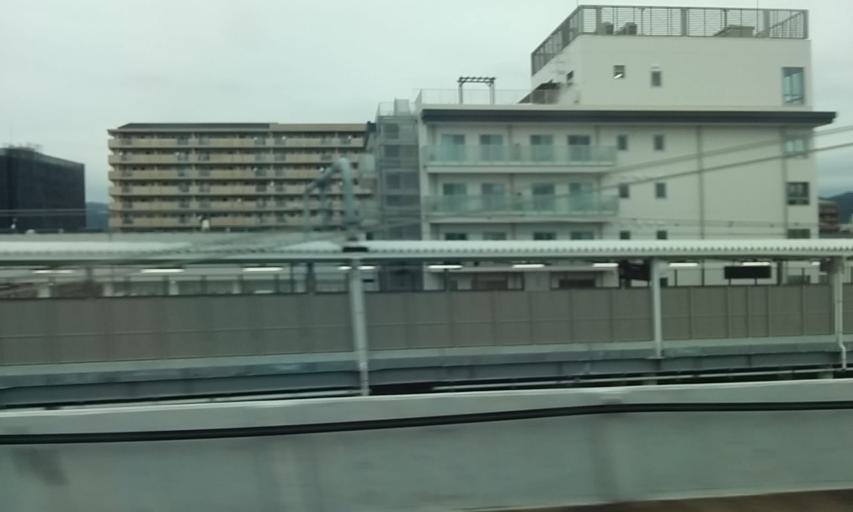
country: JP
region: Hyogo
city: Himeji
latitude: 34.8240
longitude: 134.7111
